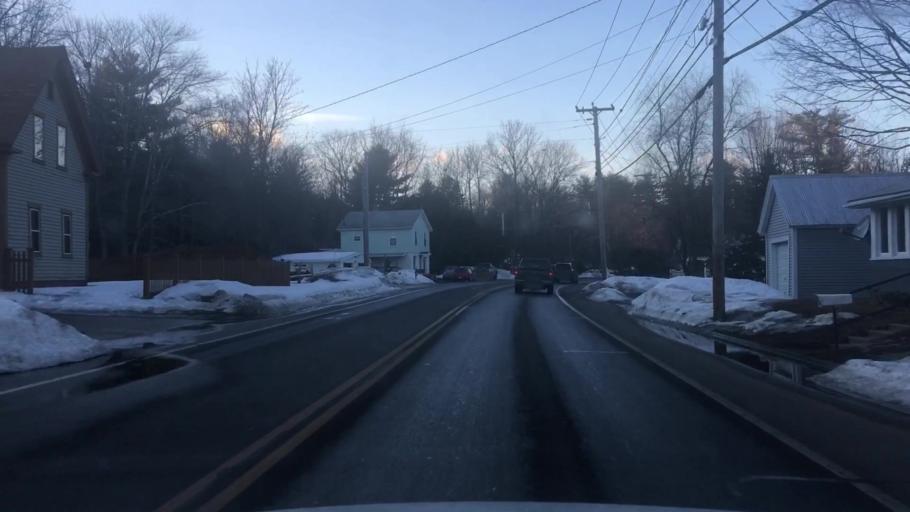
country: US
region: Maine
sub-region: York County
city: Springvale
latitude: 43.4720
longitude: -70.8088
